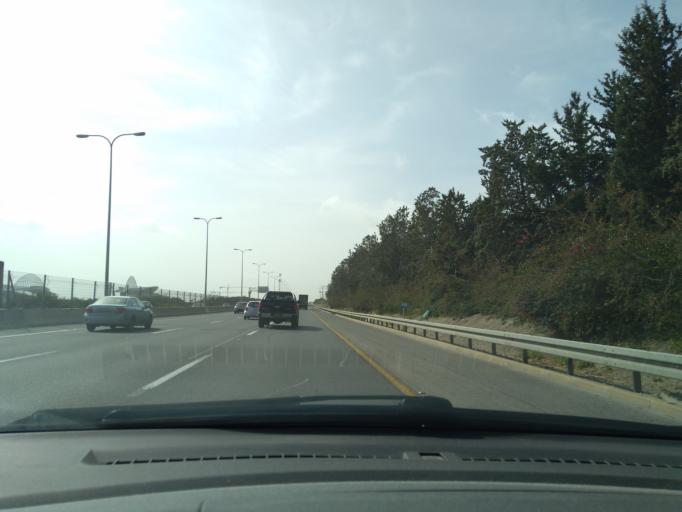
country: IL
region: Central District
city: Netanya
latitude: 32.3006
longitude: 34.8631
